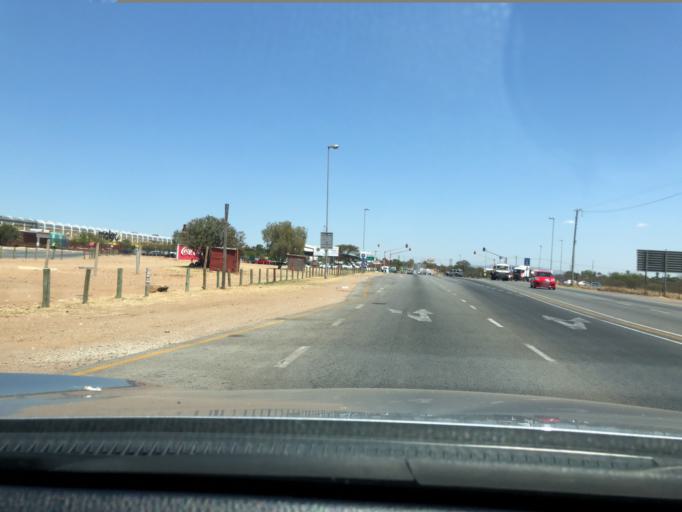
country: ZA
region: Limpopo
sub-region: Capricorn District Municipality
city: Polokwane
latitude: -23.8716
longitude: 29.4648
